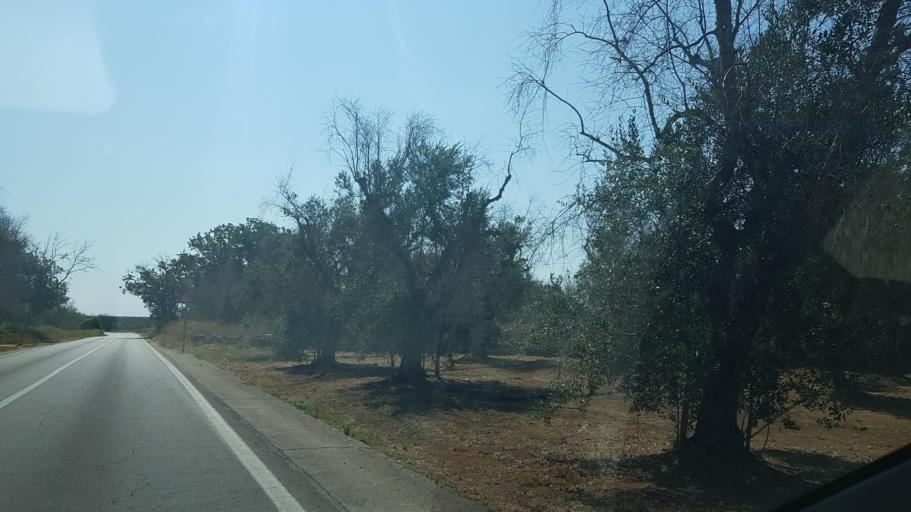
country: IT
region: Apulia
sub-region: Provincia di Lecce
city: Montesano Salentino
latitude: 40.0038
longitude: 18.2989
